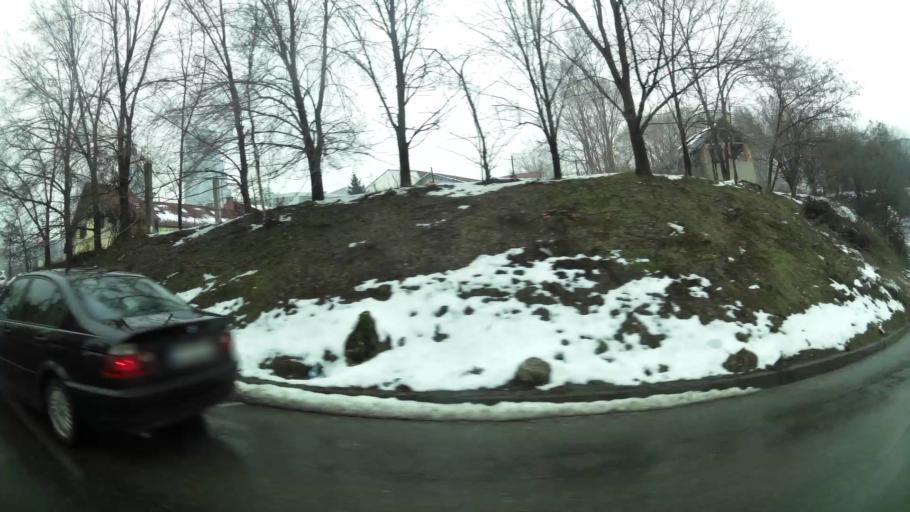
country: RS
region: Central Serbia
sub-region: Belgrade
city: Zvezdara
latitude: 44.7813
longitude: 20.5130
